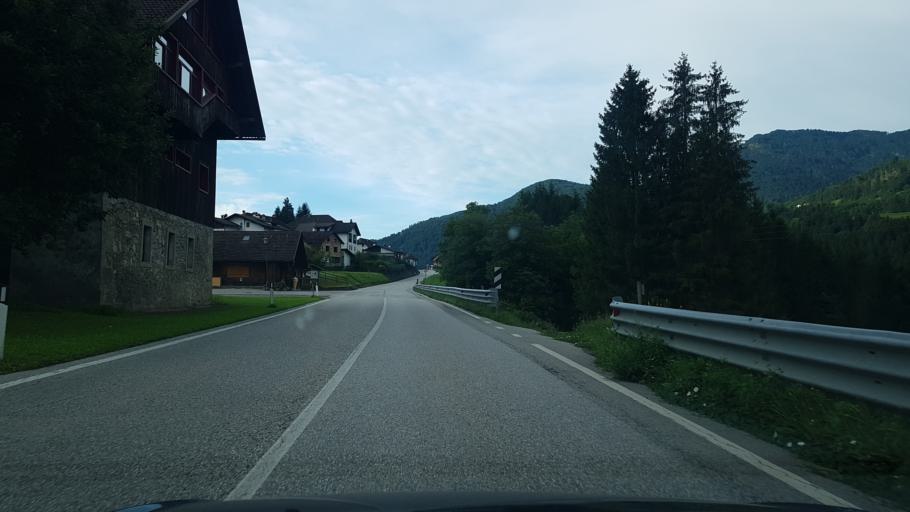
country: IT
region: Friuli Venezia Giulia
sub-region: Provincia di Udine
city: Ovaro
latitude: 46.4926
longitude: 12.8659
